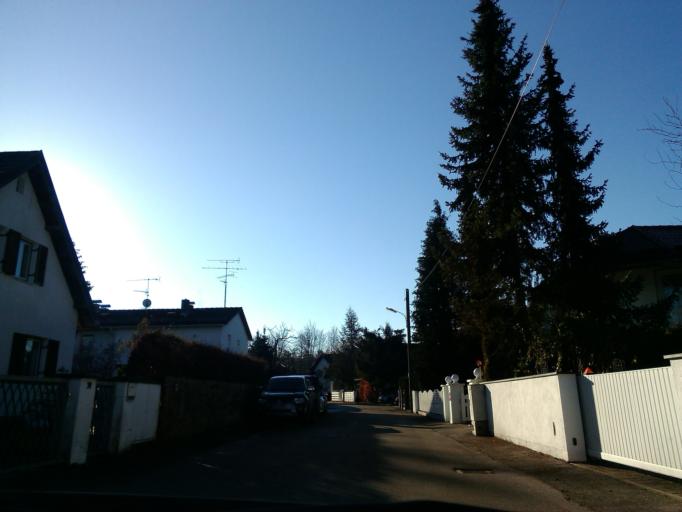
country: DE
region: Bavaria
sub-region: Upper Bavaria
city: Gauting
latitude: 48.0532
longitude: 11.3604
